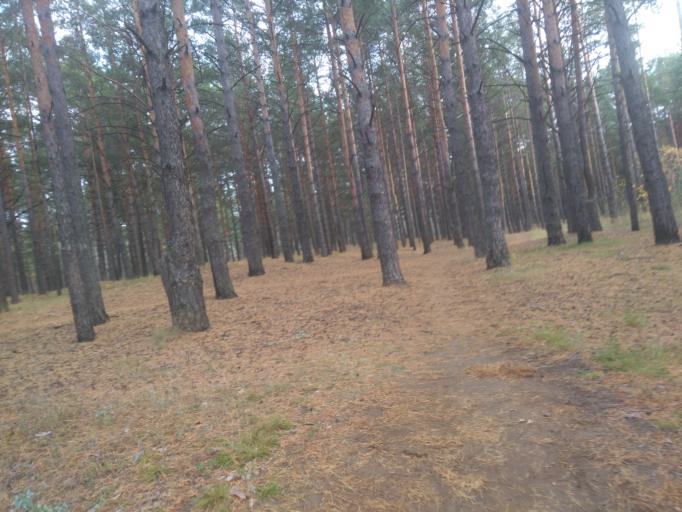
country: RU
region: Tatarstan
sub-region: Tukayevskiy Rayon
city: Naberezhnyye Chelny
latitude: 55.7548
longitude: 52.3823
